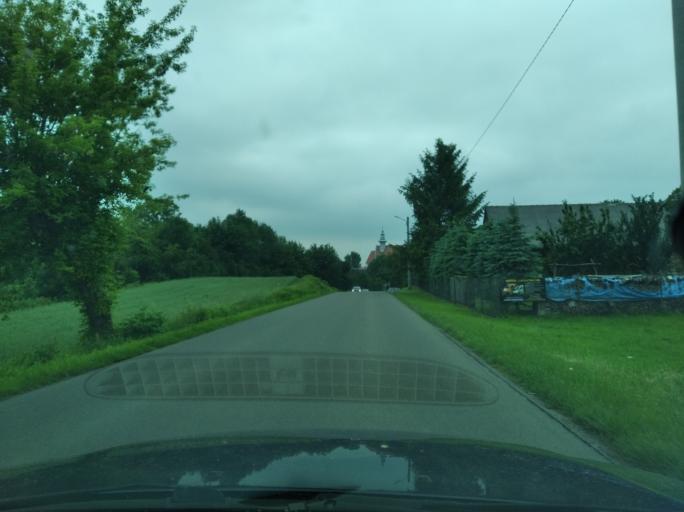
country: PL
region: Subcarpathian Voivodeship
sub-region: Powiat ropczycko-sedziszowski
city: Sedziszow Malopolski
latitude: 50.0507
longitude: 21.6886
